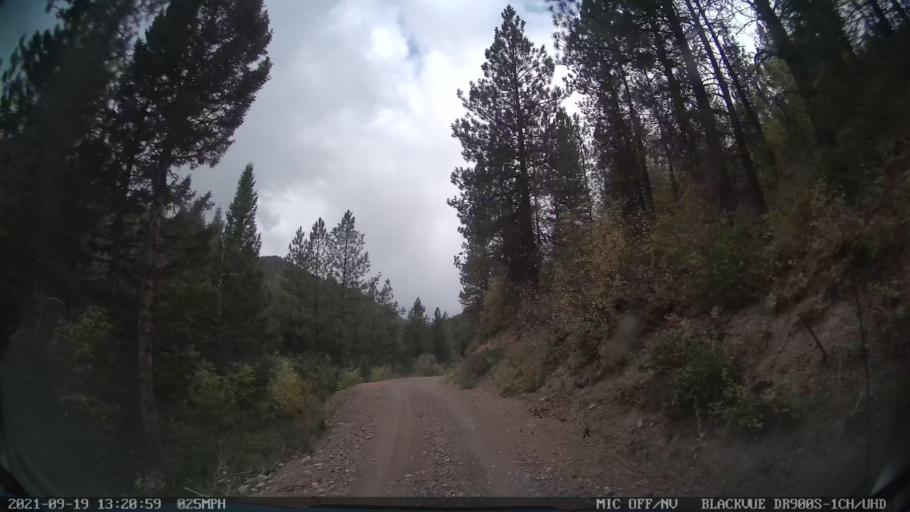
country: US
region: Montana
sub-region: Missoula County
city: Seeley Lake
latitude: 47.1669
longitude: -113.3494
